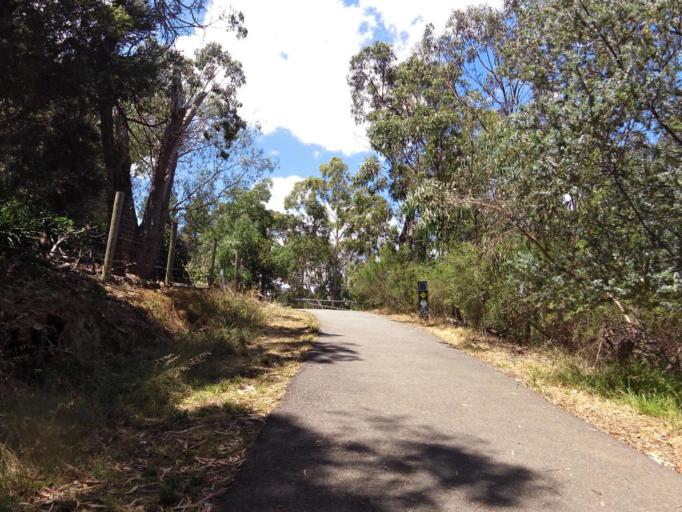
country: AU
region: Victoria
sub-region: Nillumbik
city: Research
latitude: -37.6955
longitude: 145.1739
